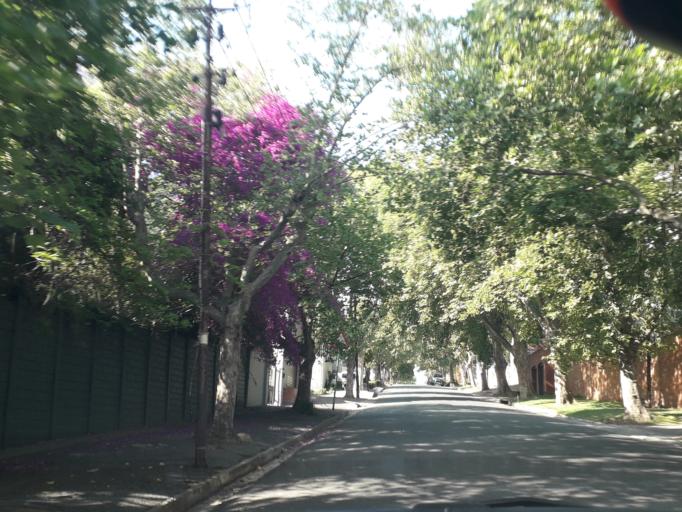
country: ZA
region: Gauteng
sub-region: City of Johannesburg Metropolitan Municipality
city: Johannesburg
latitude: -26.1473
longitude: 28.0333
